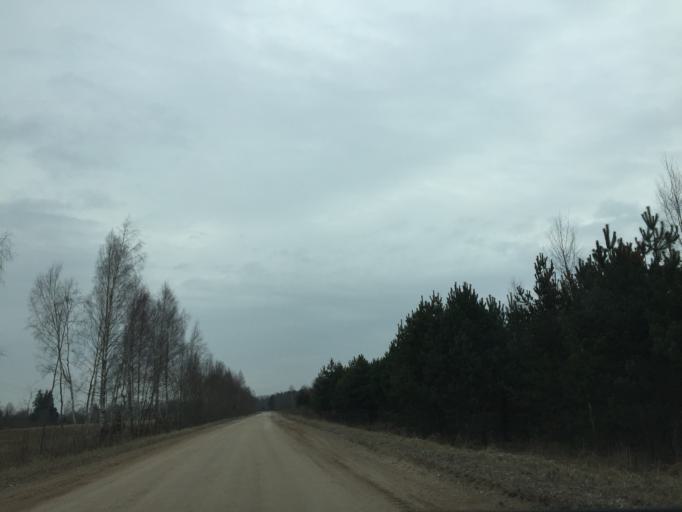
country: LV
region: Ozolnieku
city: Ozolnieki
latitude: 56.7045
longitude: 23.7553
